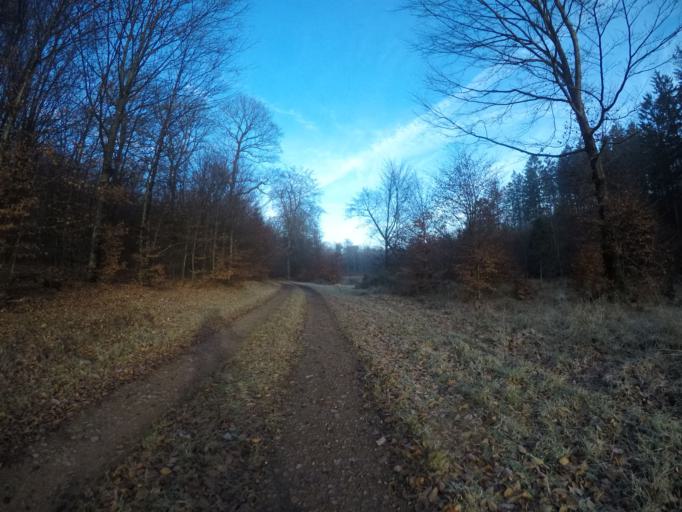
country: BE
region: Wallonia
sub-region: Province du Luxembourg
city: Habay-la-Vieille
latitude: 49.7640
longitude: 5.6593
